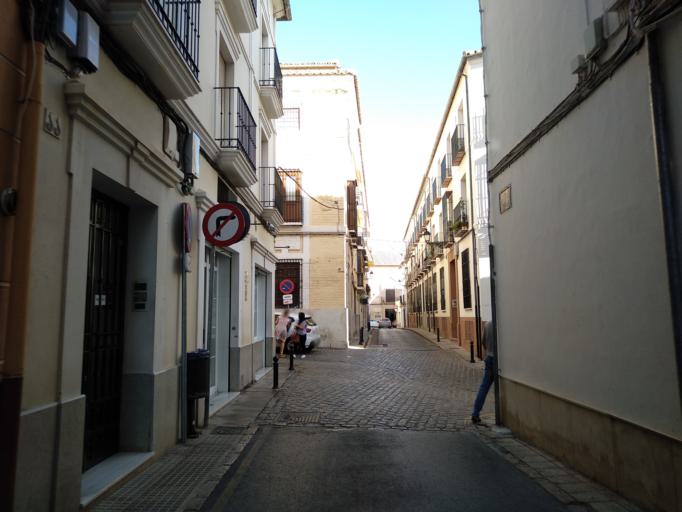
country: ES
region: Andalusia
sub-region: Provincia de Malaga
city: Antequera
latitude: 37.0167
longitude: -4.5611
